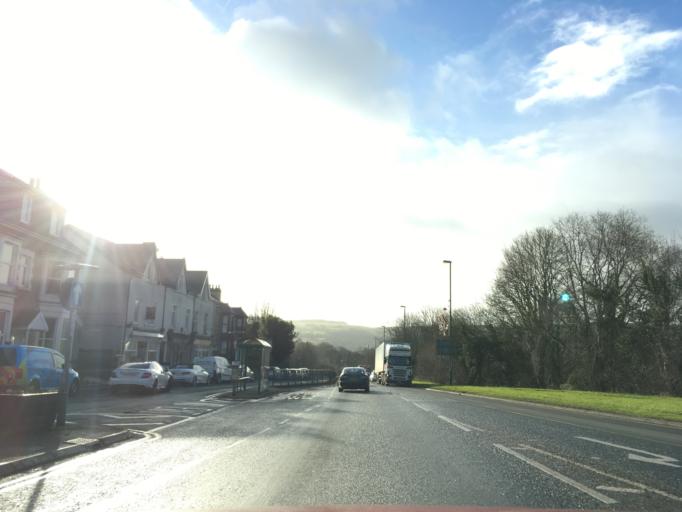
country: GB
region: Wales
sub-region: Caerphilly County Borough
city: Hengoed
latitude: 51.6452
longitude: -3.2221
